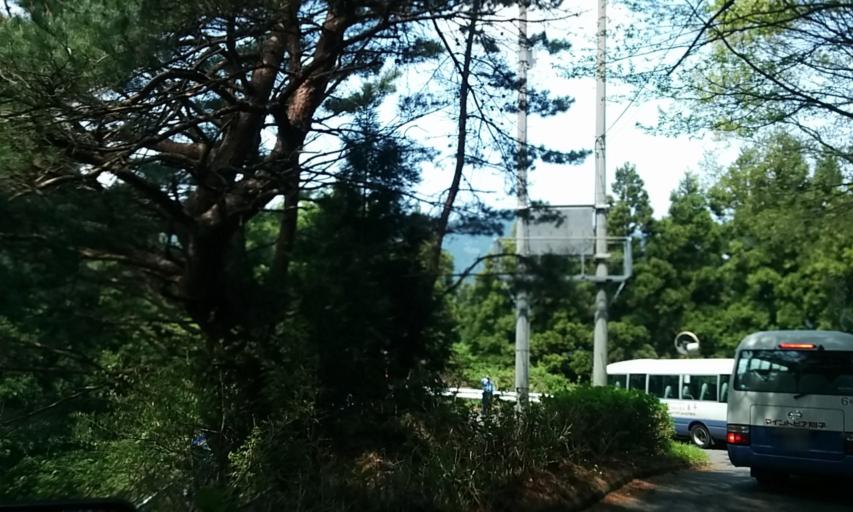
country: JP
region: Ehime
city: Niihama
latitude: 33.8792
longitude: 133.3098
